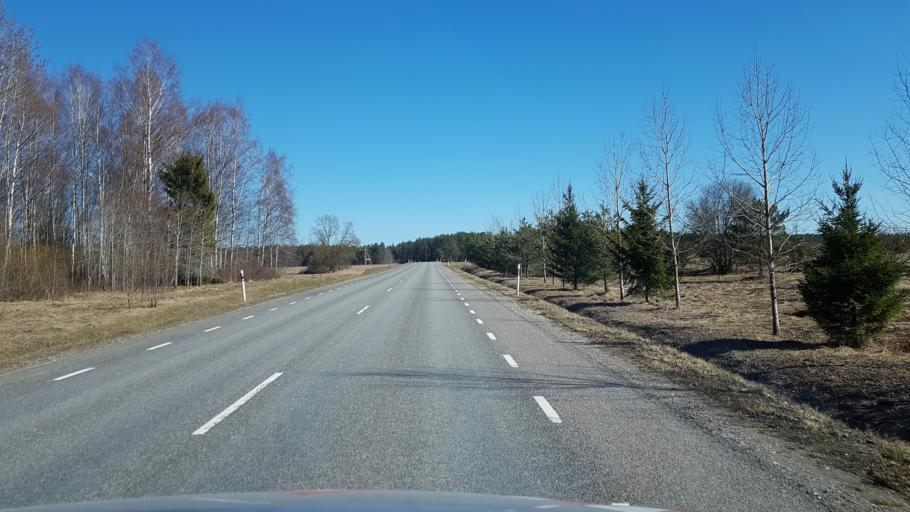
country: EE
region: Laeaene-Virumaa
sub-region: Viru-Nigula vald
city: Kunda
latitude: 59.3635
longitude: 26.6151
